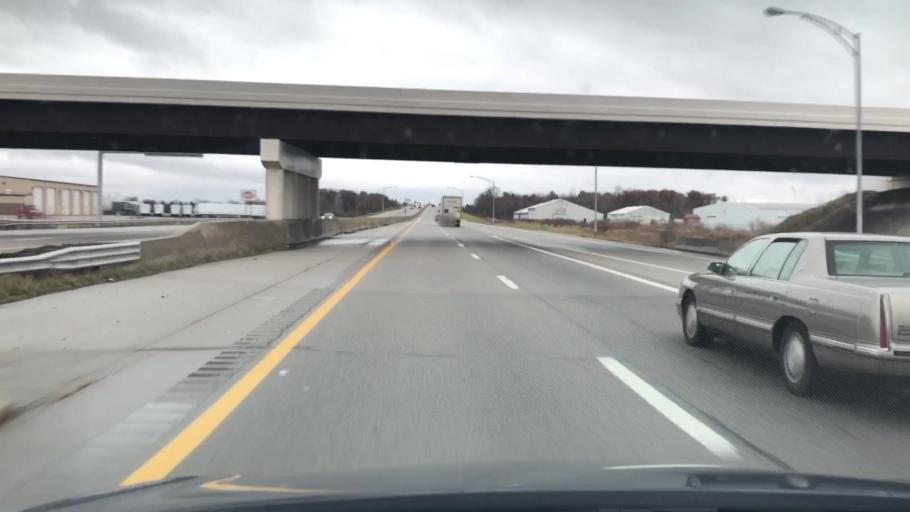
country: US
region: Ohio
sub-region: Wood County
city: Millbury
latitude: 41.5594
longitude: -83.4603
